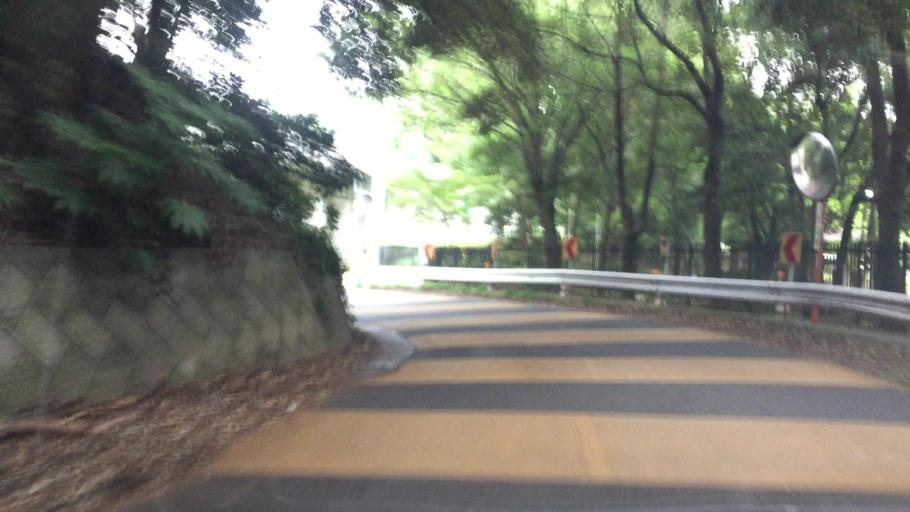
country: JP
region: Chiba
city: Matsudo
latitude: 35.7985
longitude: 139.9371
